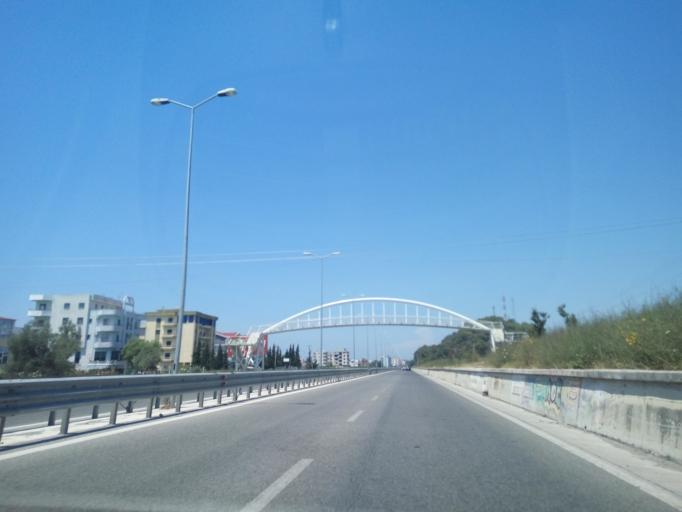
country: AL
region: Tirane
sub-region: Rrethi i Kavajes
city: Golem
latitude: 41.2247
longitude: 19.5273
